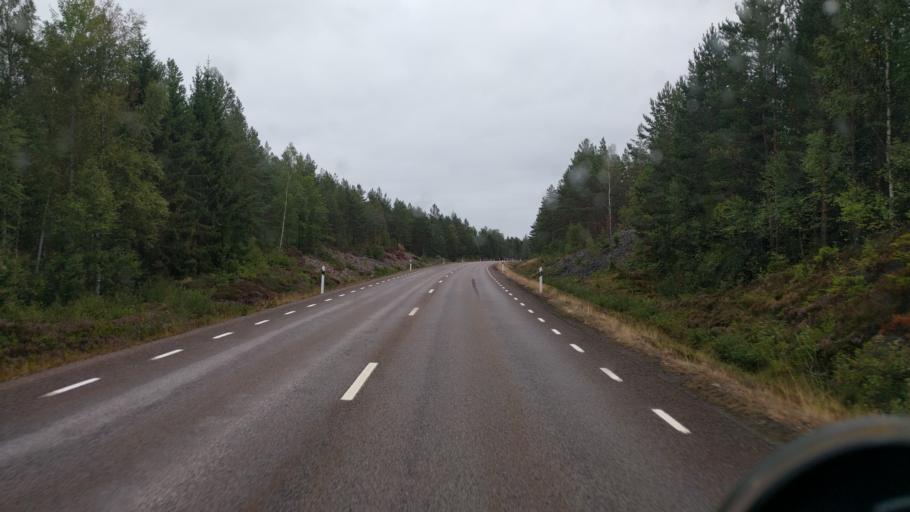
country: SE
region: Kalmar
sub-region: Vasterviks Kommun
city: Ankarsrum
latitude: 57.7048
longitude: 16.2002
